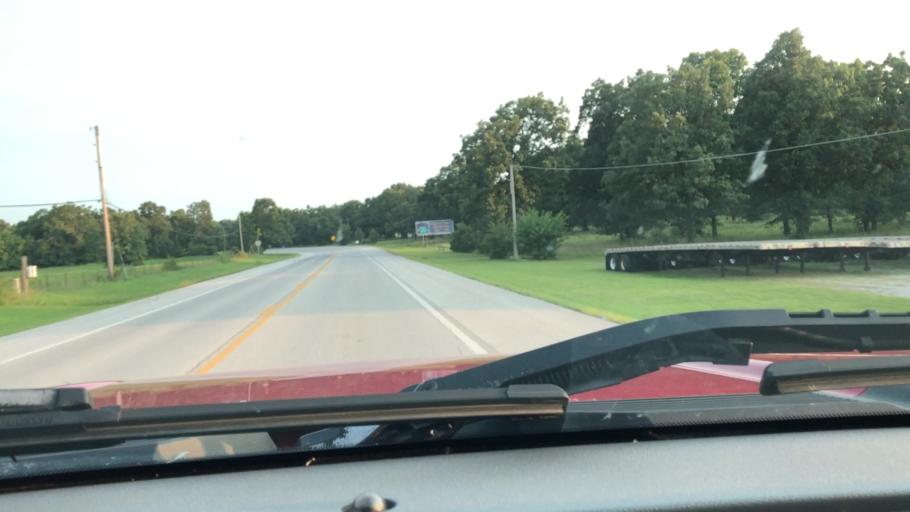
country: US
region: Missouri
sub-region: Jasper County
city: Duquesne
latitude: 36.9822
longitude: -94.4641
